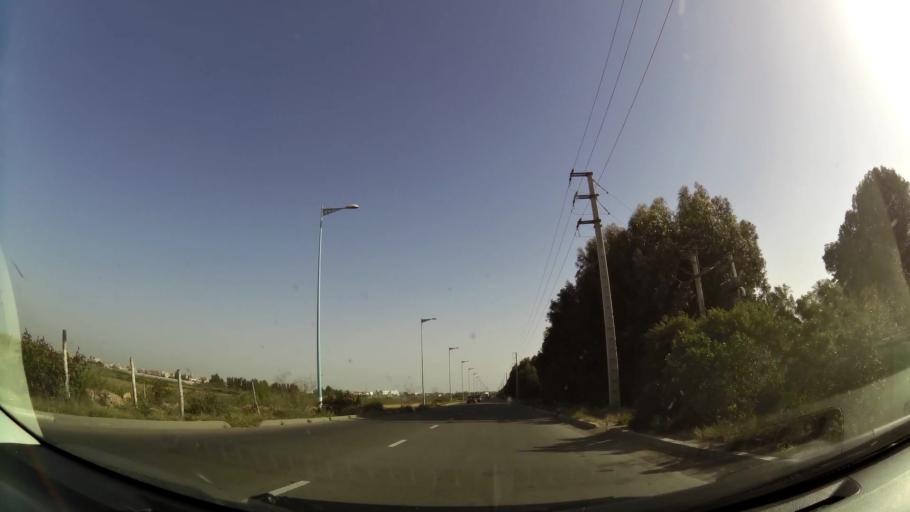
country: MA
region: Souss-Massa-Draa
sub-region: Inezgane-Ait Mellou
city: Inezgane
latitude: 30.3595
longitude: -9.5060
